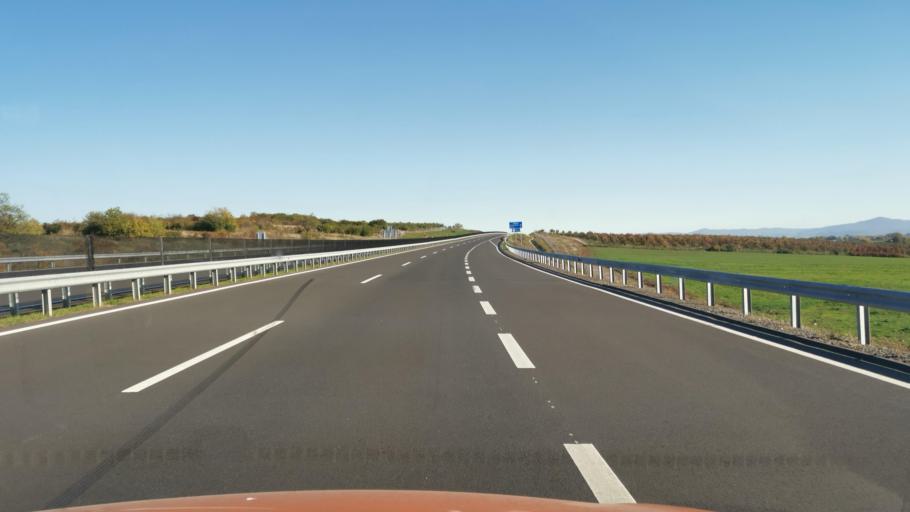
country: HU
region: Borsod-Abauj-Zemplen
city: Halmaj
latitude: 48.2553
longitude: 20.9807
